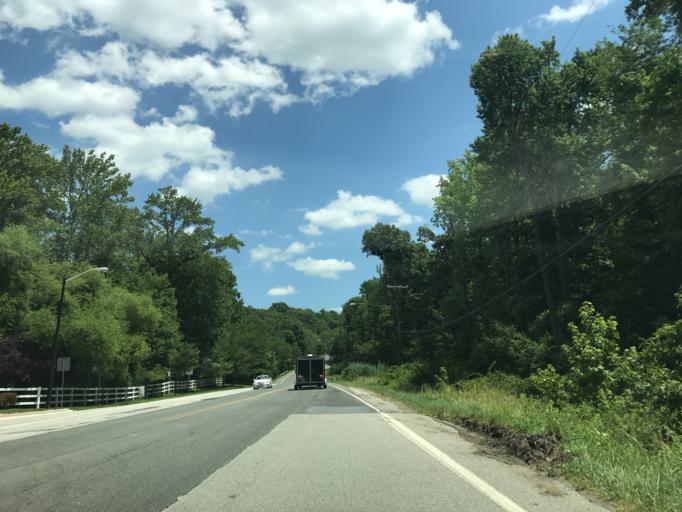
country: US
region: Maryland
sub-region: Prince George's County
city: South Laurel
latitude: 39.0590
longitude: -76.8793
